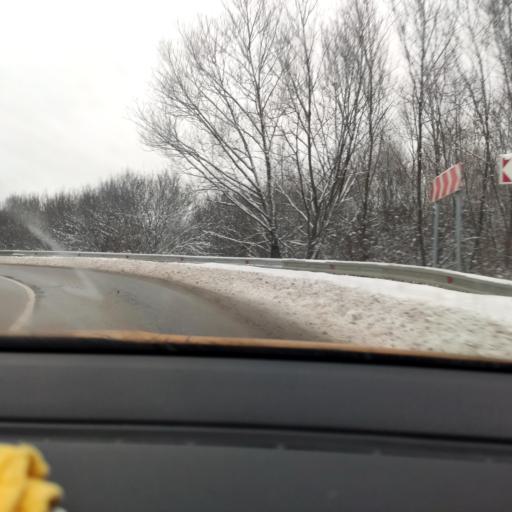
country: RU
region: Moskovskaya
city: Yershovo
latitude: 55.7522
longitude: 36.8742
